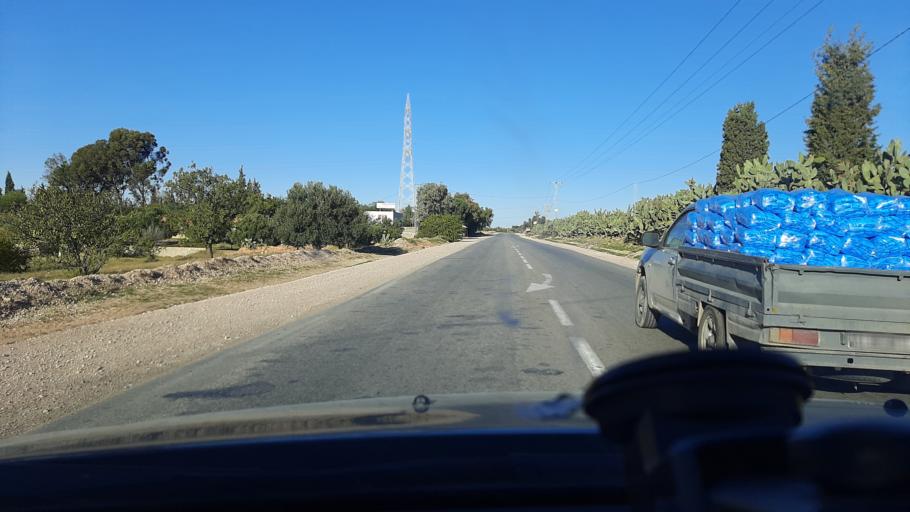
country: TN
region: Safaqis
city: Sfax
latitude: 34.8102
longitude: 10.6218
